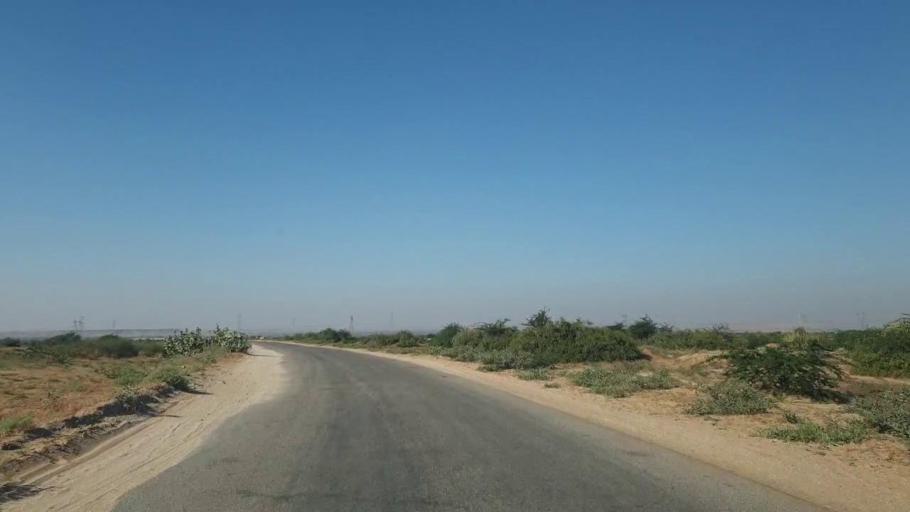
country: PK
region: Sindh
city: Gharo
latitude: 25.1665
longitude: 67.6620
